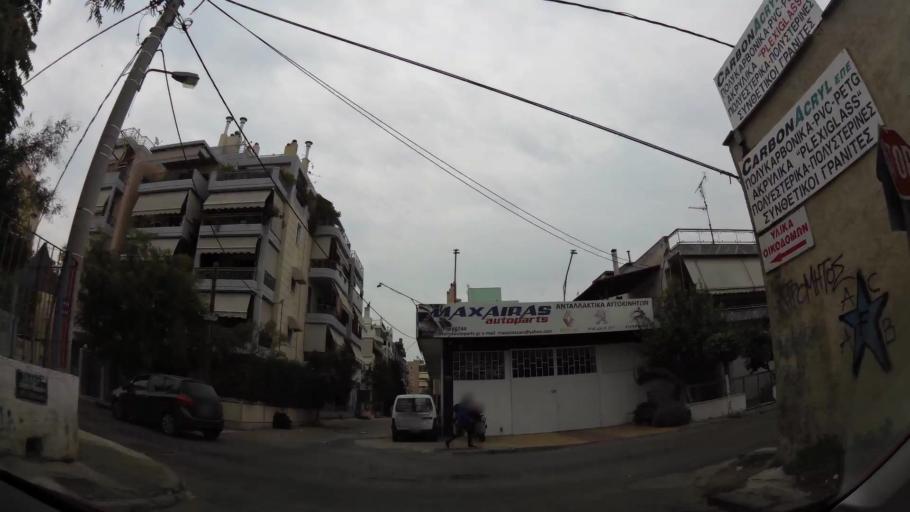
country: GR
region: Attica
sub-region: Nomarchia Athinas
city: Agioi Anargyroi
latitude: 38.0136
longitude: 23.7129
